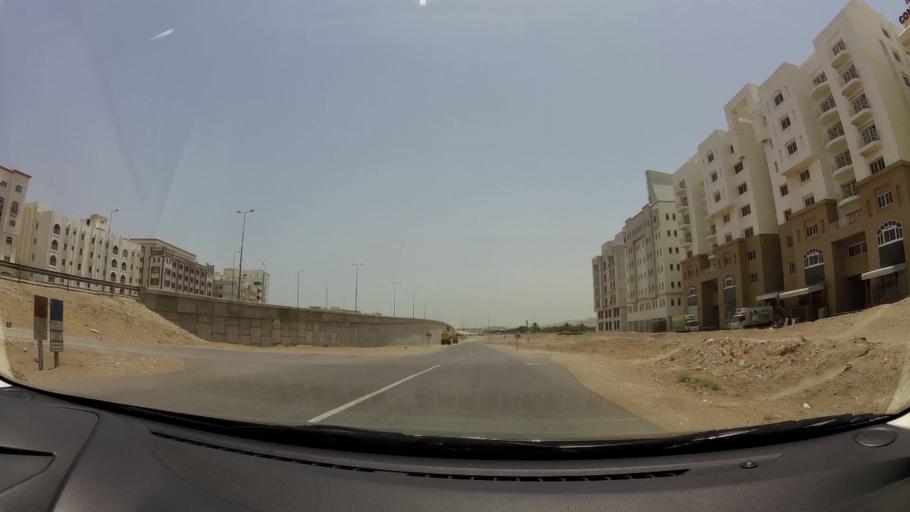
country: OM
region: Muhafazat Masqat
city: Bawshar
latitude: 23.5849
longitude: 58.4266
